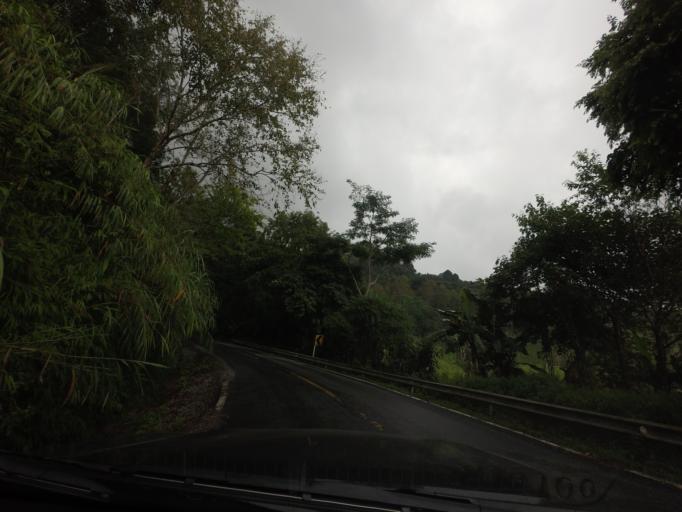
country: TH
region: Nan
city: Bo Kluea
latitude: 19.1814
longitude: 101.0802
